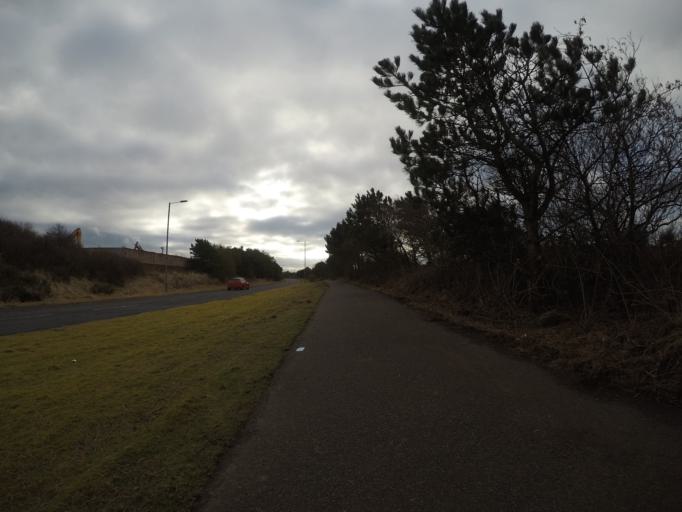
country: GB
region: Scotland
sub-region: North Ayrshire
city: Irvine
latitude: 55.5993
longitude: -4.6785
